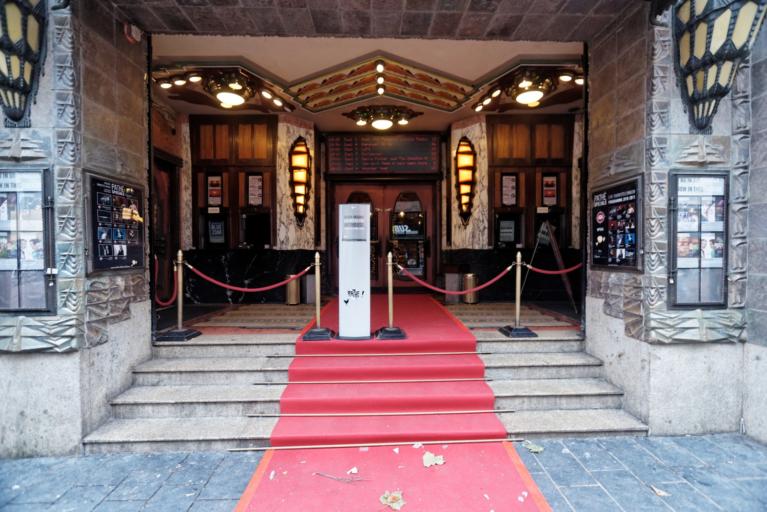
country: NL
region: North Holland
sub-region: Gemeente Amsterdam
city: Amsterdam
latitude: 52.3665
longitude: 4.8947
